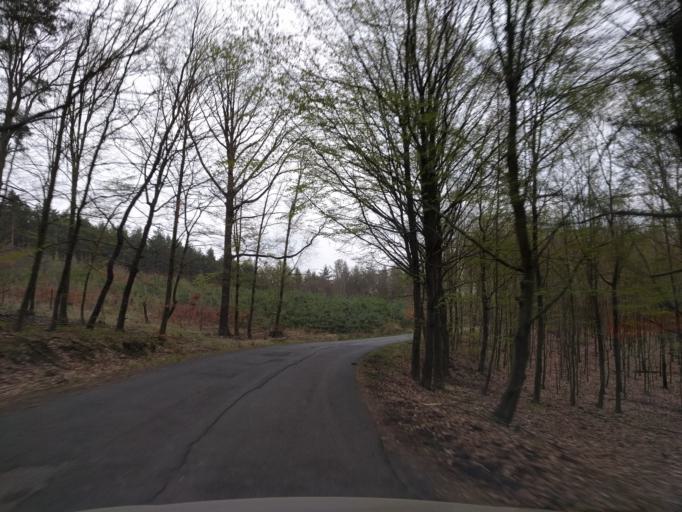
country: CZ
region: Central Bohemia
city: Kostelec nad Cernymi Lesy
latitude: 50.0112
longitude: 14.8331
